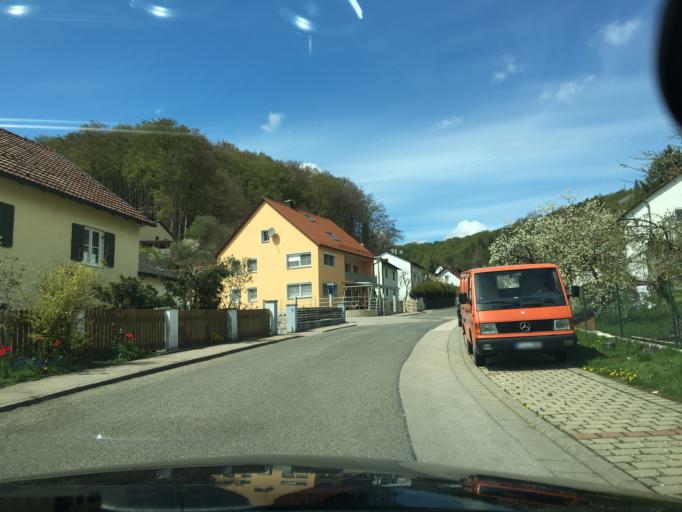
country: DE
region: Bavaria
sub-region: Regierungsbezirk Mittelfranken
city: Solnhofen
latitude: 48.8706
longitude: 11.0031
